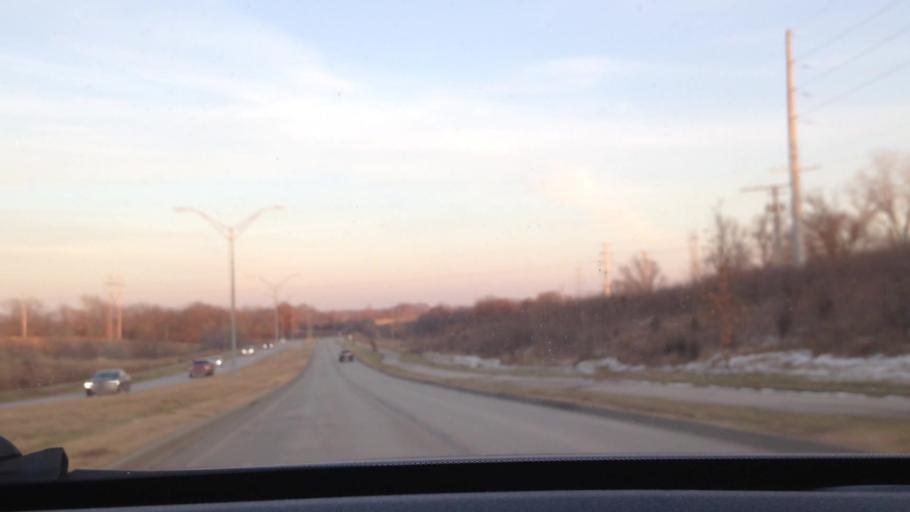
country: US
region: Missouri
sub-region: Clay County
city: Pleasant Valley
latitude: 39.2093
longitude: -94.4613
